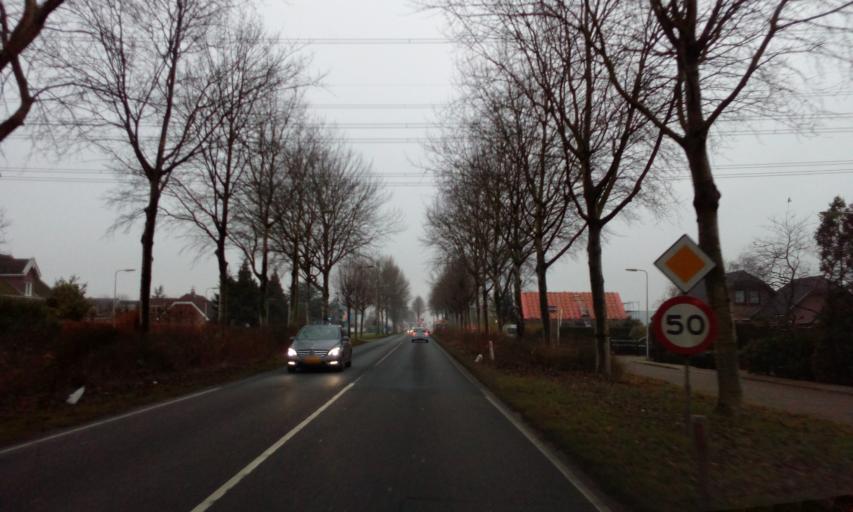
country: NL
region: South Holland
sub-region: Gemeente Capelle aan den IJssel
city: Capelle aan den IJssel
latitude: 51.9625
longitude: 4.5899
